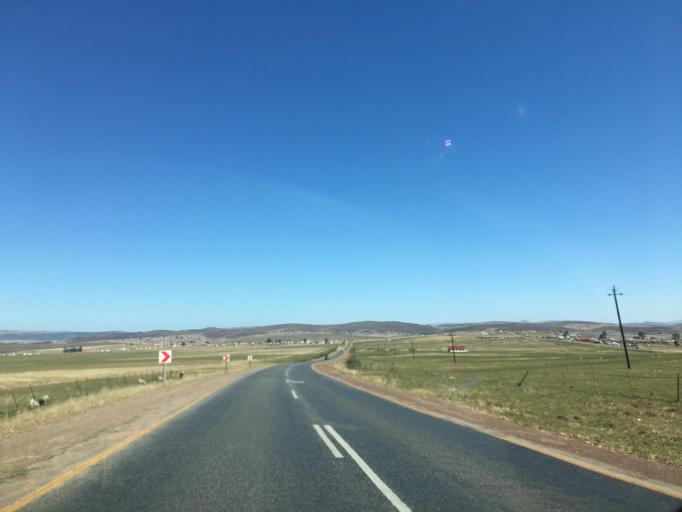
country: ZA
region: Eastern Cape
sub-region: Chris Hani District Municipality
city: Cofimvaba
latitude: -31.9432
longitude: 27.8360
